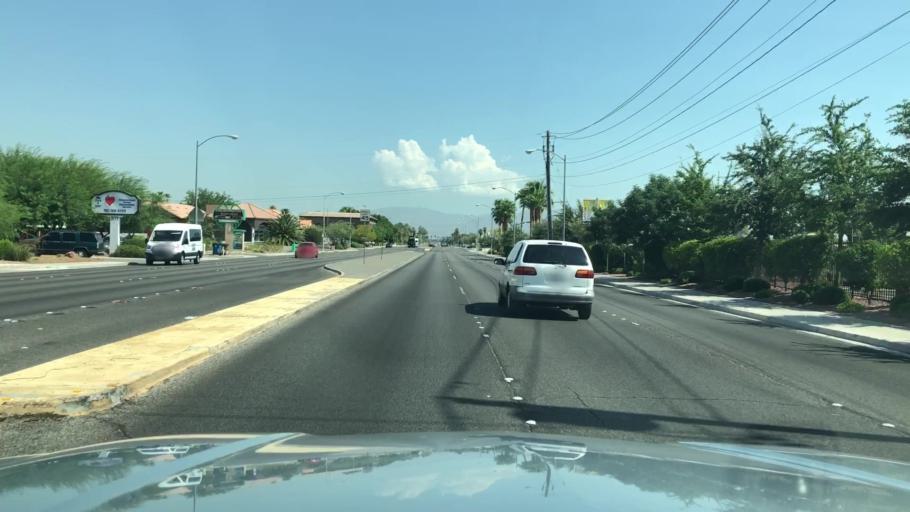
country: US
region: Nevada
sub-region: Clark County
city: Spring Valley
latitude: 36.1311
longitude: -115.2249
